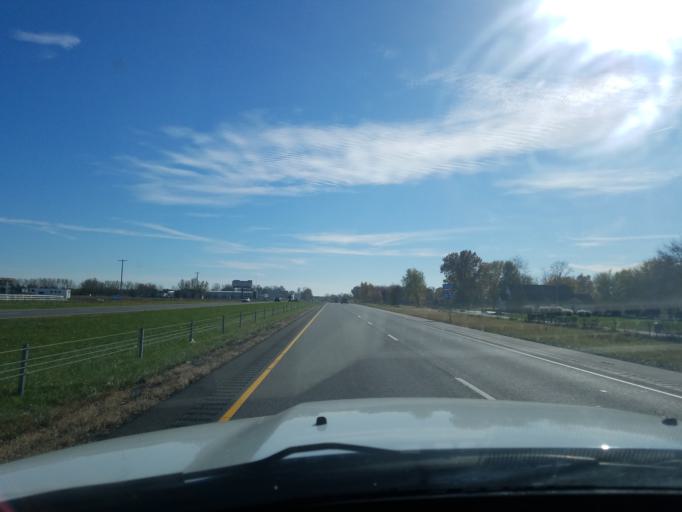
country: US
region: Indiana
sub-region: Jackson County
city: Seymour
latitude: 38.9512
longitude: -85.8428
